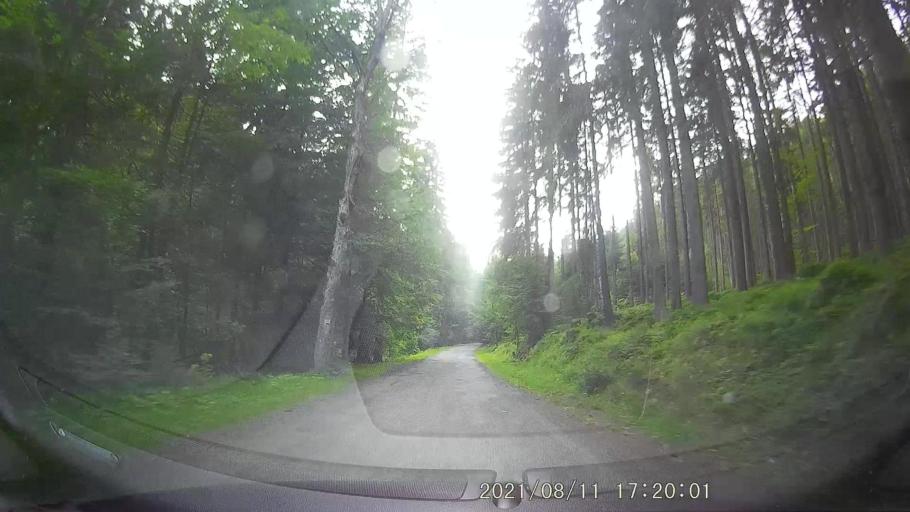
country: PL
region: Lower Silesian Voivodeship
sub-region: Powiat klodzki
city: Polanica-Zdroj
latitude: 50.3067
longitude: 16.5159
